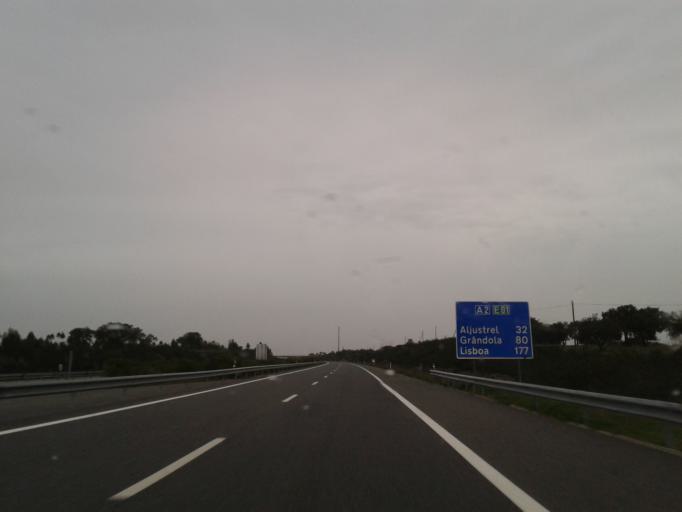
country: PT
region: Beja
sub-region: Ourique
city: Ourique
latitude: 37.6747
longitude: -8.1603
